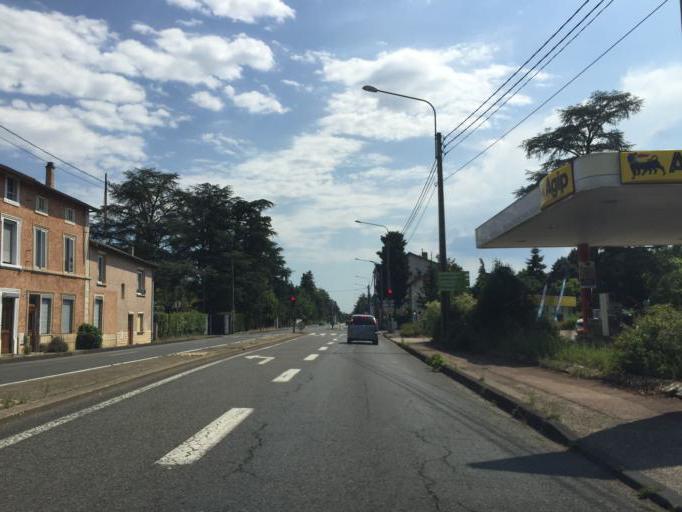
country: FR
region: Rhone-Alpes
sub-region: Departement du Rhone
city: Charbonnieres-les-Bains
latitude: 45.7792
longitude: 4.7510
